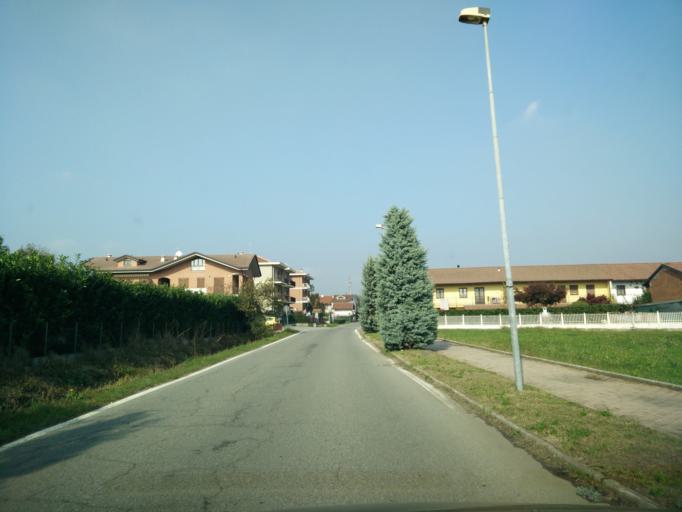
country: IT
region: Piedmont
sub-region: Provincia di Torino
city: Leini
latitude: 45.2023
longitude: 7.7166
